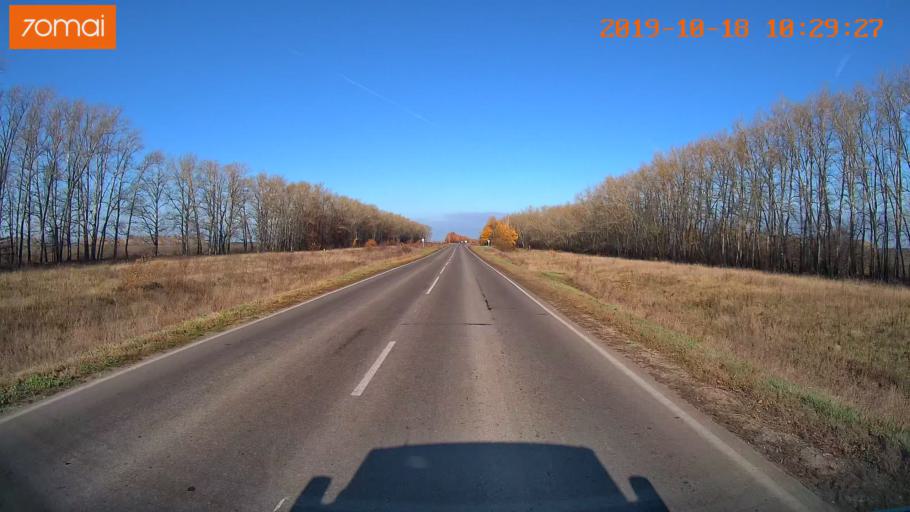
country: RU
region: Tula
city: Kurkino
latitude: 53.4514
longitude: 38.6564
